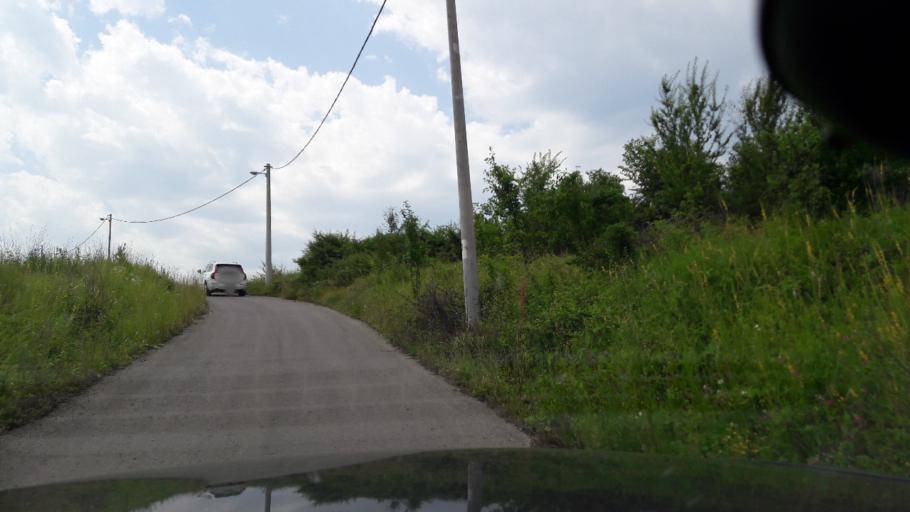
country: RS
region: Central Serbia
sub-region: Belgrade
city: Sopot
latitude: 44.6219
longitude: 20.6014
